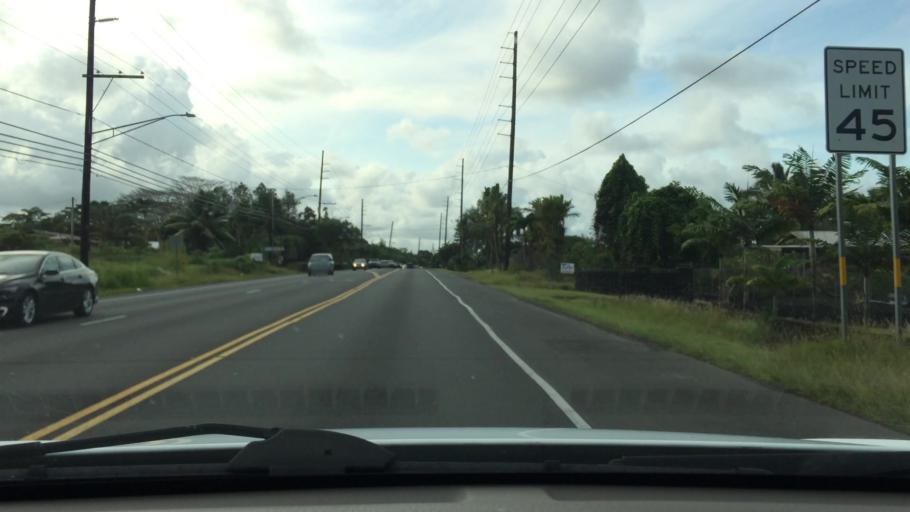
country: US
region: Hawaii
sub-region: Hawaii County
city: Orchidlands Estates
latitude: 19.5705
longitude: -154.9999
